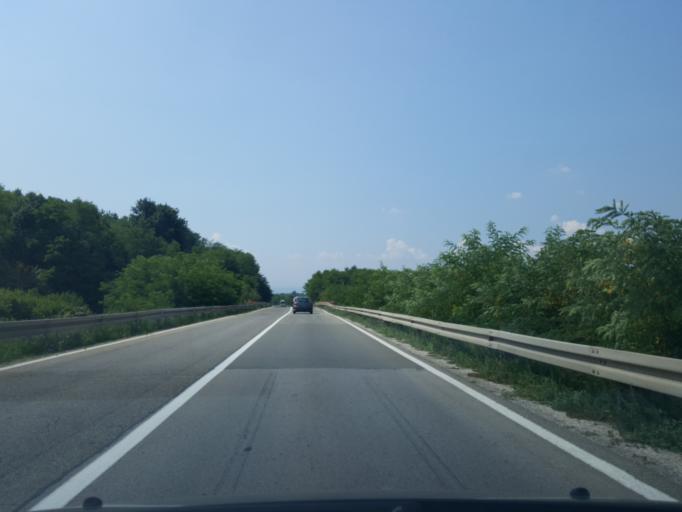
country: RS
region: Central Serbia
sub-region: Belgrade
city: Sopot
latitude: 44.5366
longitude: 20.6576
